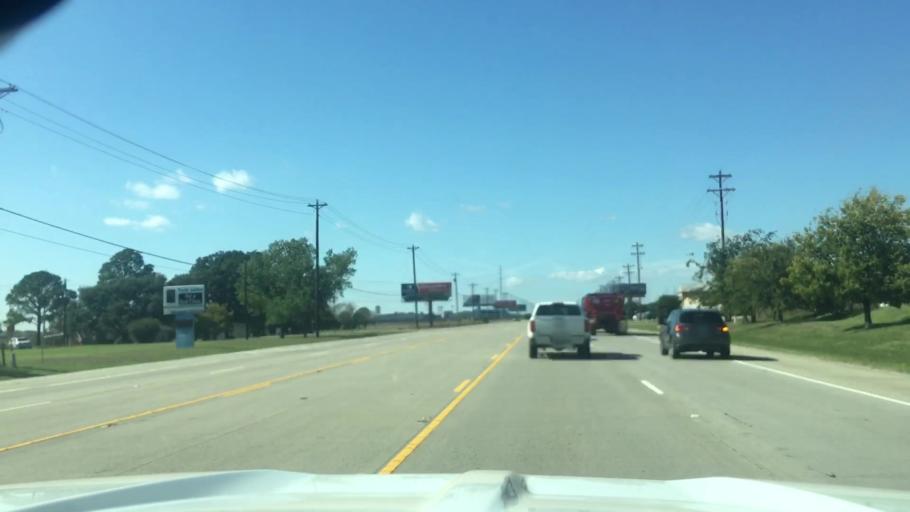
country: US
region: Texas
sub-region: Denton County
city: Little Elm
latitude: 33.2199
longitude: -96.9095
